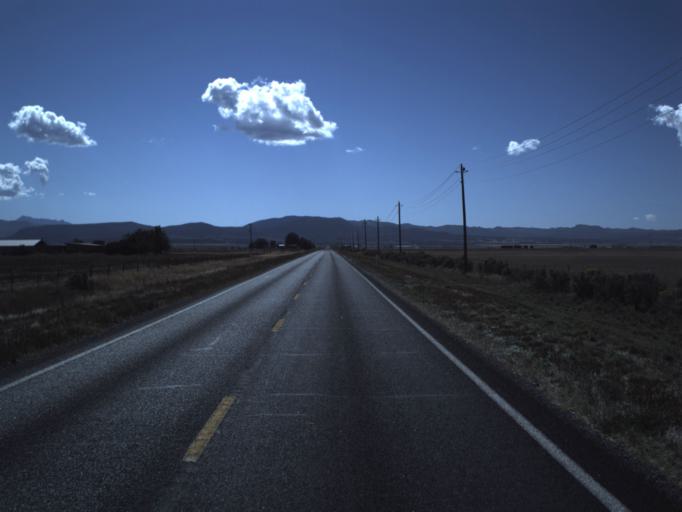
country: US
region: Utah
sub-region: Washington County
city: Enterprise
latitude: 37.6585
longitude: -113.6612
